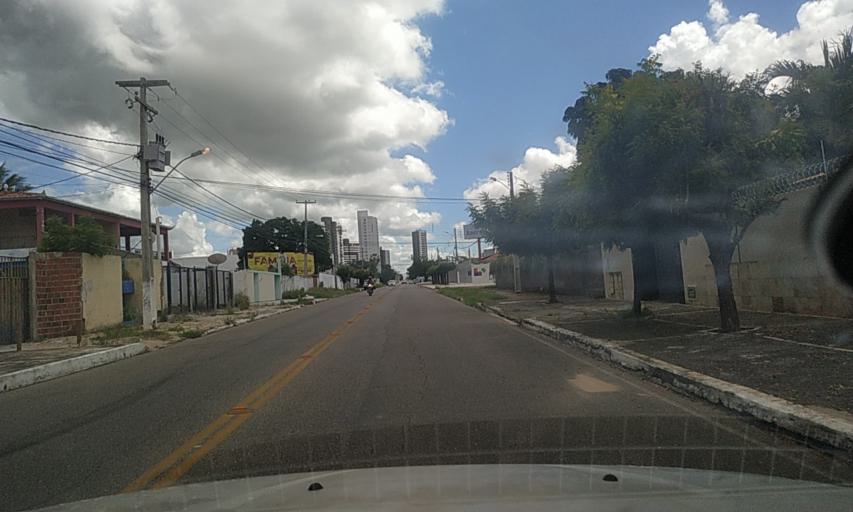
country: BR
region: Rio Grande do Norte
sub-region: Mossoro
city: Mossoro
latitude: -5.1833
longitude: -37.3549
